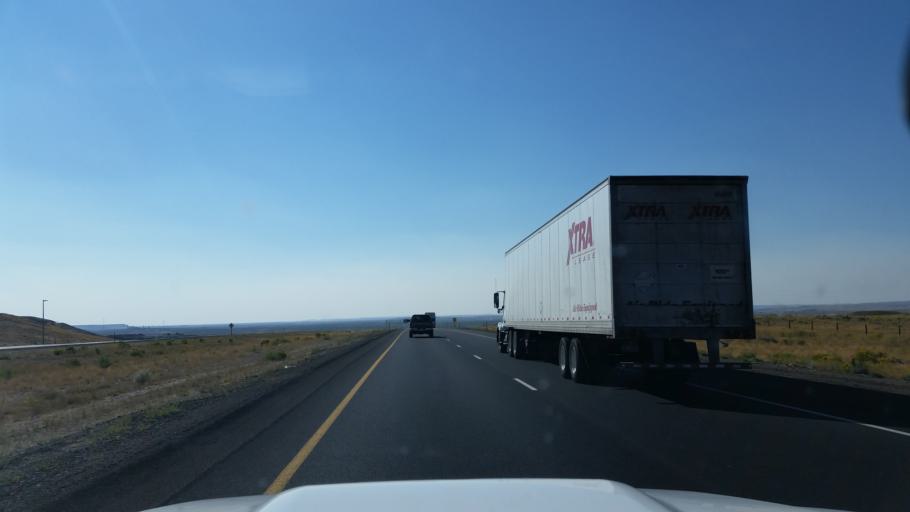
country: US
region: Wyoming
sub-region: Sweetwater County
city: Green River
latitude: 41.5429
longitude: -109.8958
